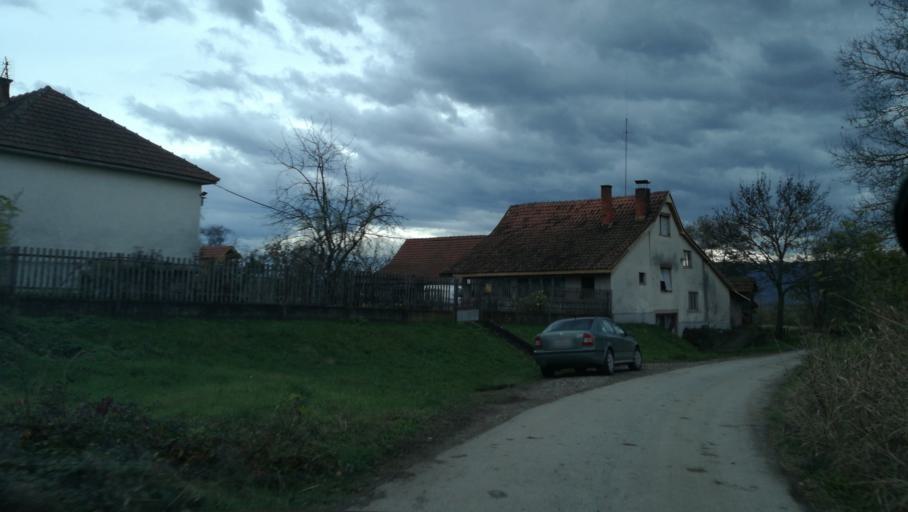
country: RS
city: Prislonica
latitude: 43.9117
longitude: 20.4289
